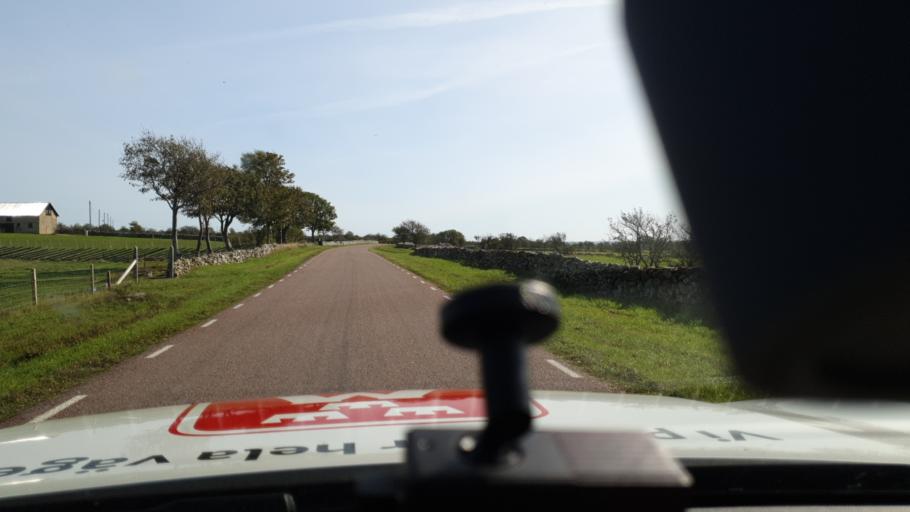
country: SE
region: Gotland
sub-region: Gotland
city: Hemse
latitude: 56.9207
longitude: 18.1386
